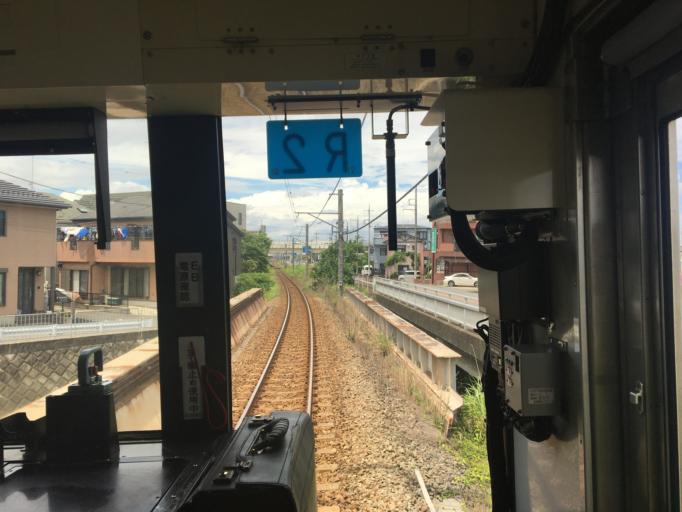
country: JP
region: Kanagawa
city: Atsugi
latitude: 35.4047
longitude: 139.3814
